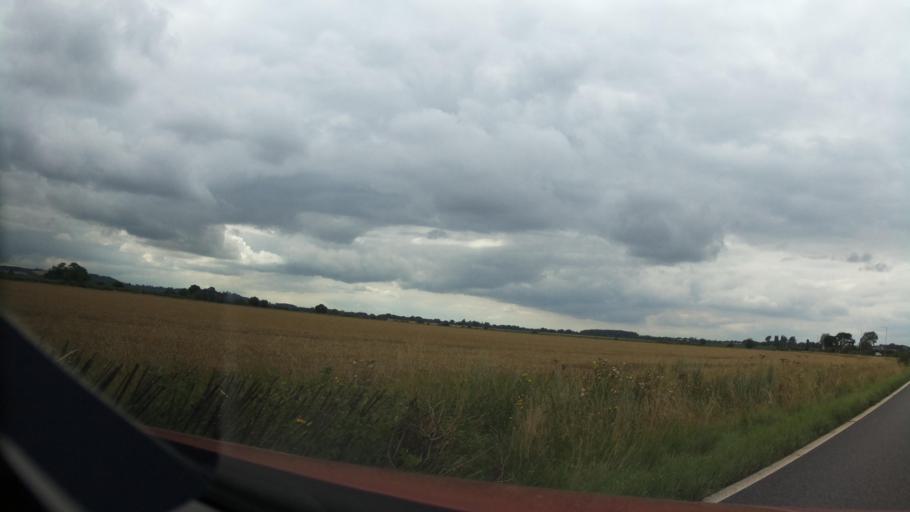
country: GB
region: England
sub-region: Lincolnshire
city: Barrowby
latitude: 52.9272
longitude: -0.7029
